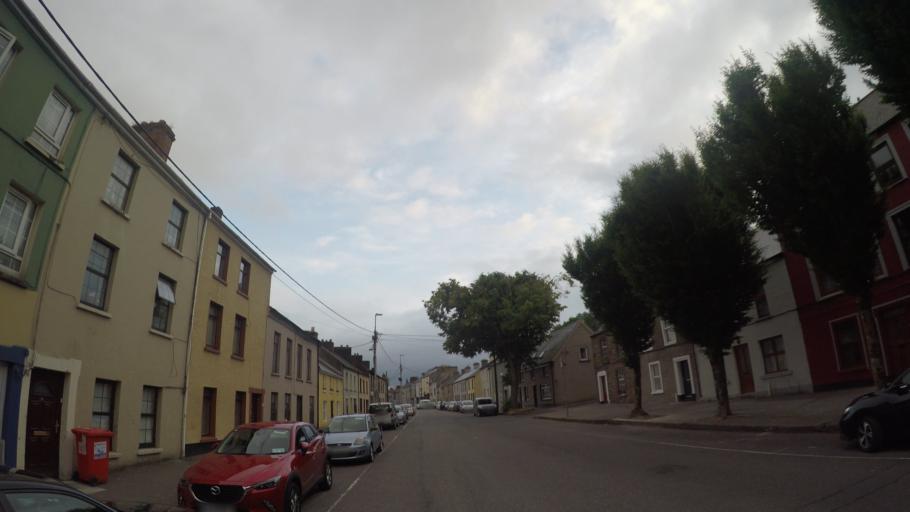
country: IE
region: Munster
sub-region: County Cork
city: Cork
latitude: 51.9151
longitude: -8.4814
